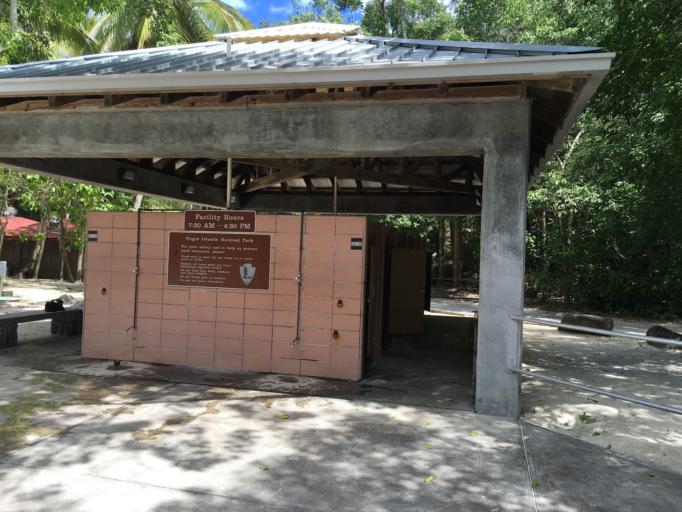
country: VI
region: Saint John Island
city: Cruz Bay
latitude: 18.3528
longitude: -64.7677
